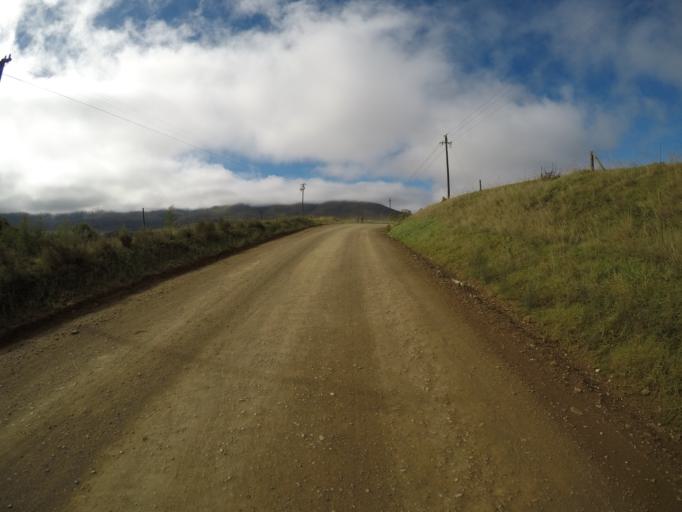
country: ZA
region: Western Cape
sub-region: Cape Winelands District Municipality
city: Ashton
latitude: -34.1305
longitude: 19.8521
